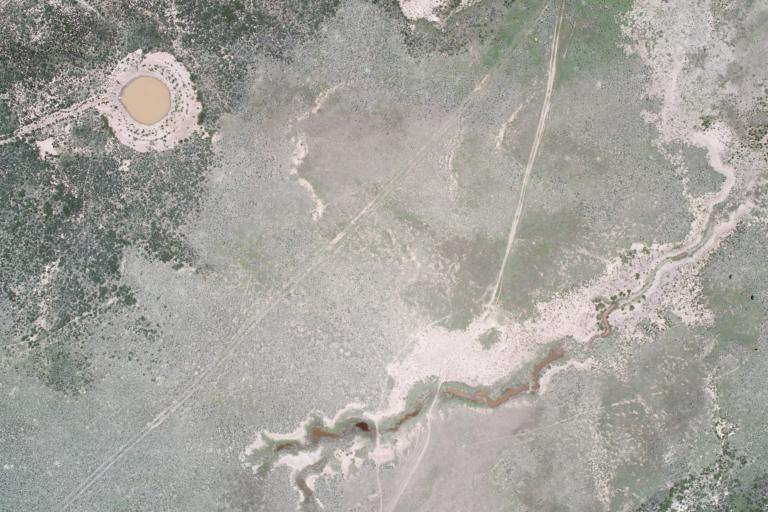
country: BO
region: La Paz
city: Patacamaya
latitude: -17.2799
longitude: -68.4985
